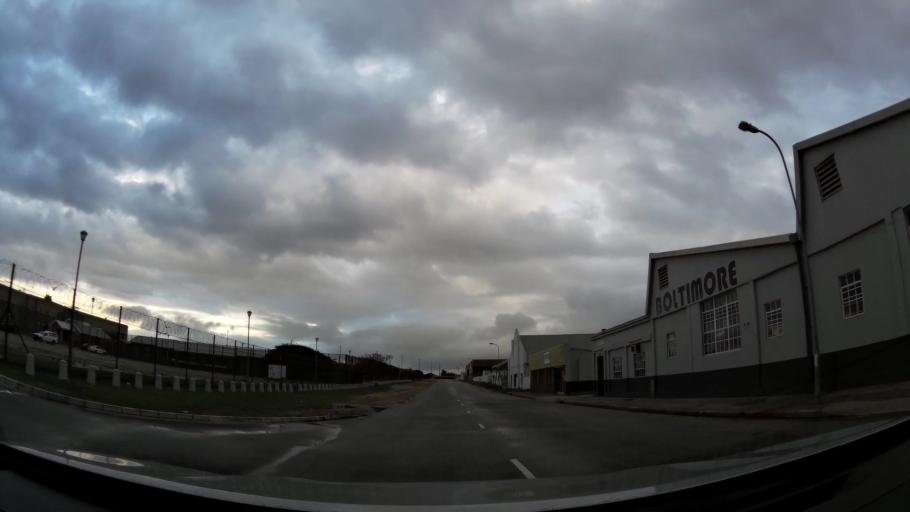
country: ZA
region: Eastern Cape
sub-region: Nelson Mandela Bay Metropolitan Municipality
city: Port Elizabeth
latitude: -33.9271
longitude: 25.6073
